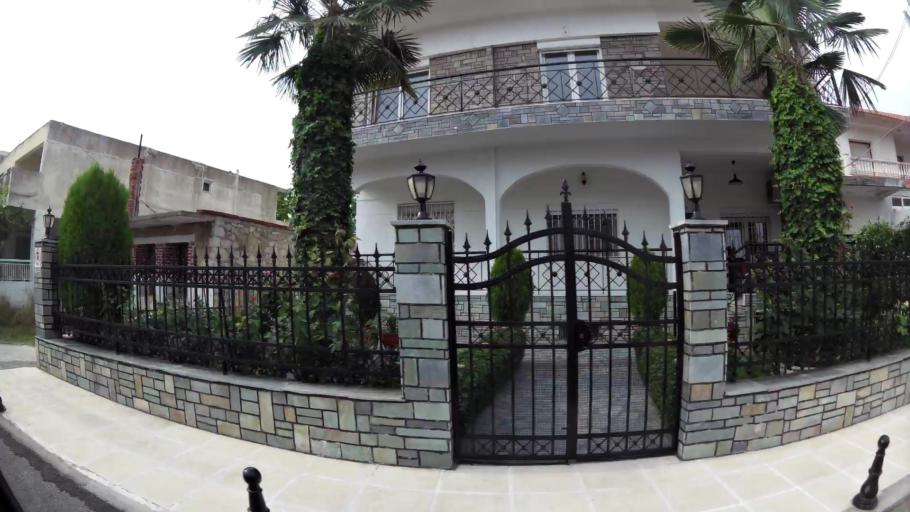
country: GR
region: Central Macedonia
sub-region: Nomos Thessalonikis
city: Oraiokastro
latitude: 40.7363
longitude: 22.9207
